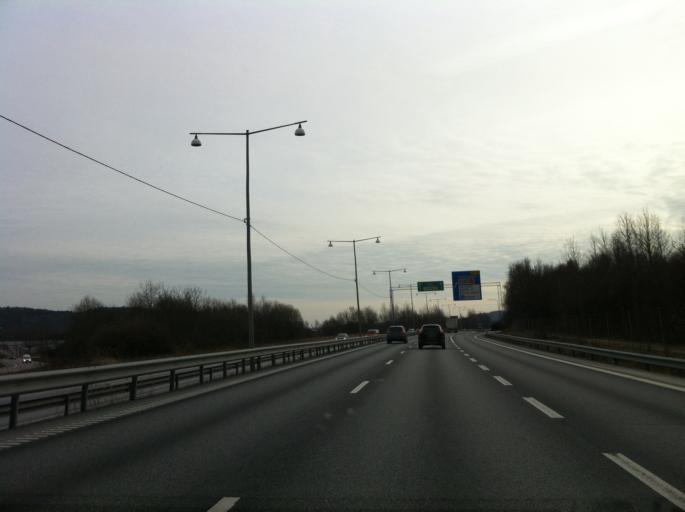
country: SE
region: Vaestra Goetaland
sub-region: Kungalvs Kommun
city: Kungalv
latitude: 57.8591
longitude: 11.9856
